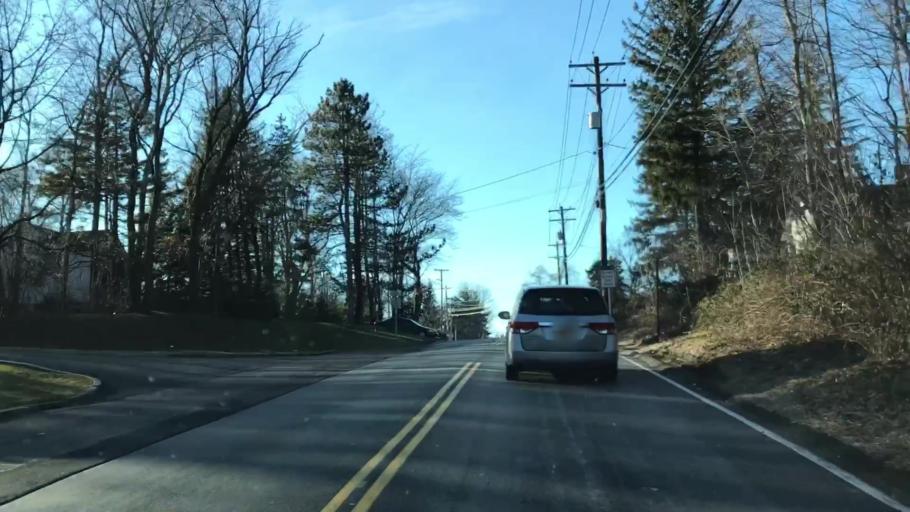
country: US
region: New York
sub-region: Rockland County
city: New Hempstead
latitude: 41.1495
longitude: -74.0314
